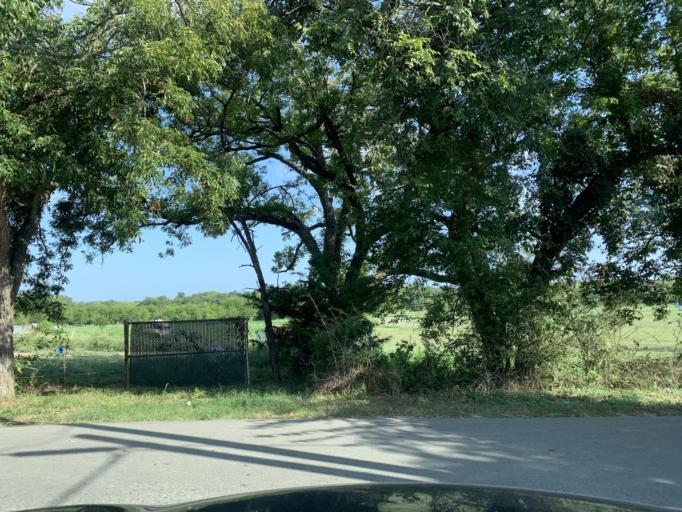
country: US
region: Texas
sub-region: Dallas County
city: Hutchins
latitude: 32.6770
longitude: -96.7825
